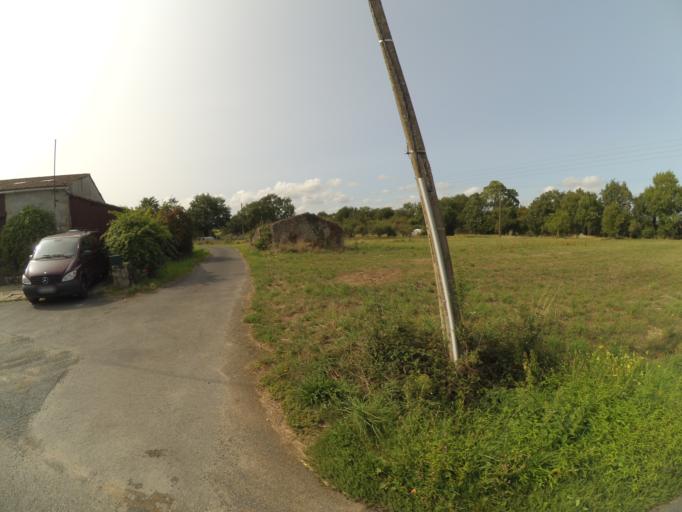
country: FR
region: Pays de la Loire
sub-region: Departement de la Loire-Atlantique
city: Boussay
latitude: 47.0239
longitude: -1.1548
